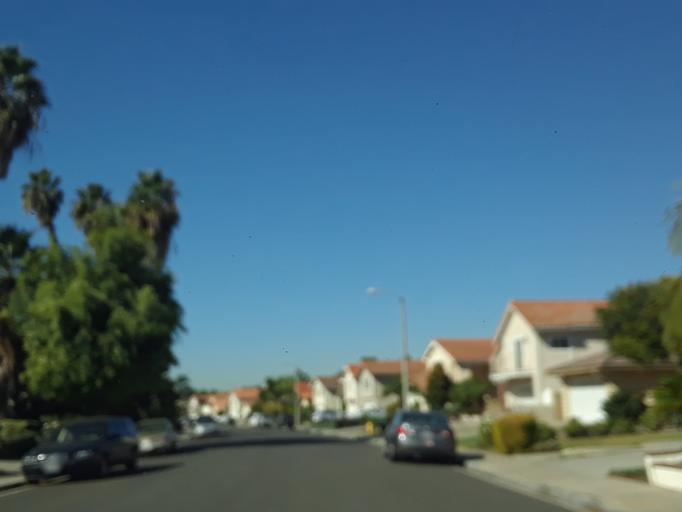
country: US
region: California
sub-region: Orange County
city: Tustin
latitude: 33.7091
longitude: -117.7936
